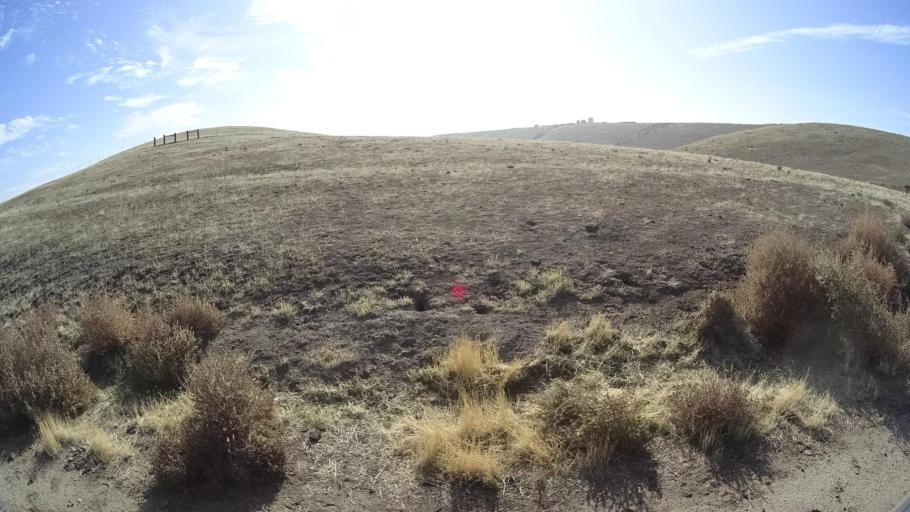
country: US
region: California
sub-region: Kern County
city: Oildale
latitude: 35.4960
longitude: -118.8562
